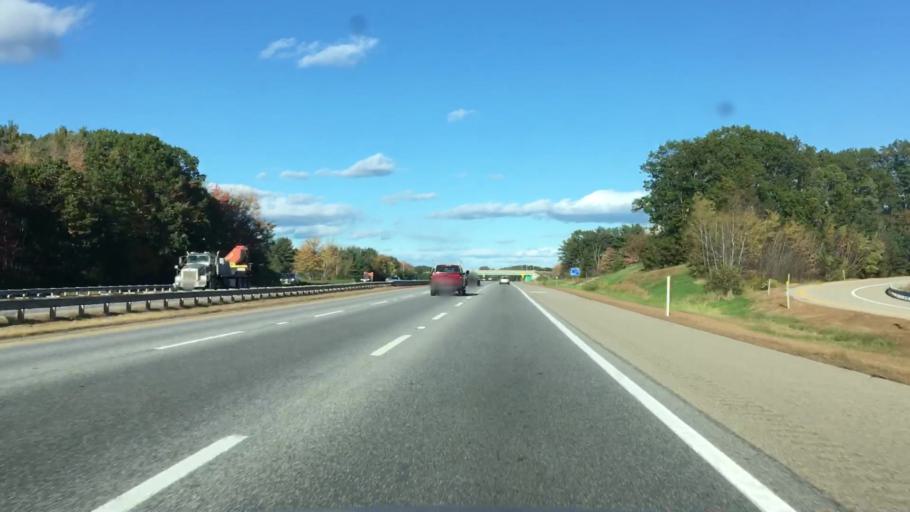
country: US
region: Maine
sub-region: York County
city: Saco
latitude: 43.5187
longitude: -70.4643
